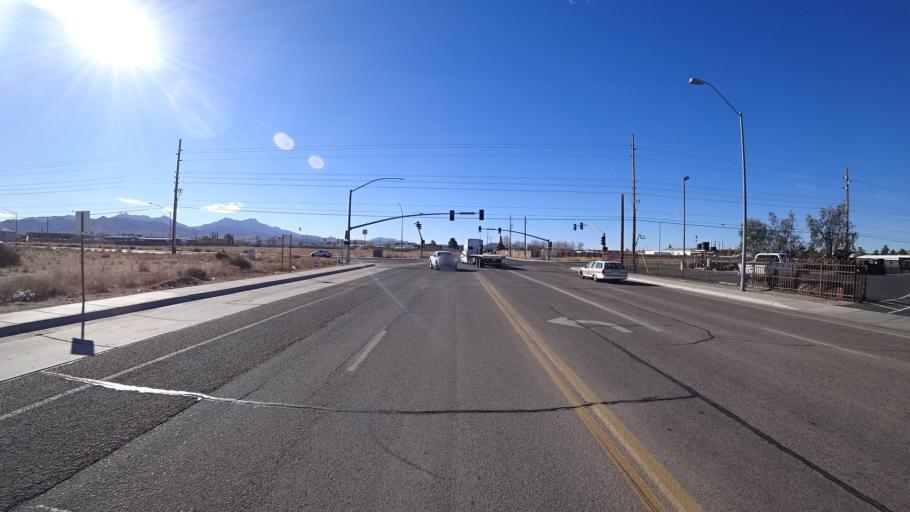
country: US
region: Arizona
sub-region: Mohave County
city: New Kingman-Butler
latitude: 35.2254
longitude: -114.0114
